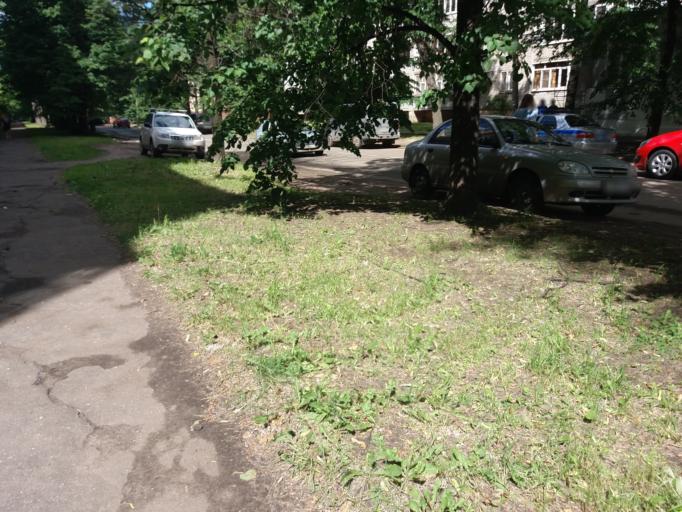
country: RU
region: Jaroslavl
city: Yaroslavl
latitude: 57.6405
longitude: 39.8395
